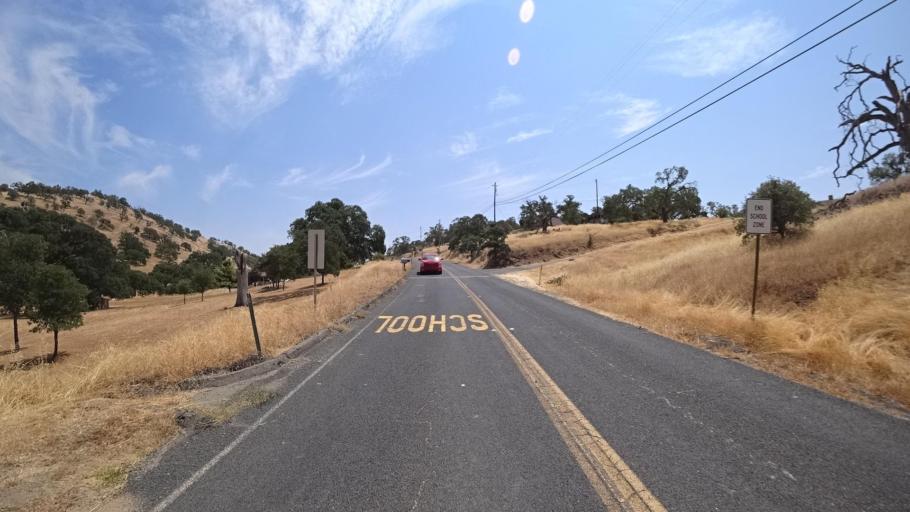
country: US
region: California
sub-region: Tuolumne County
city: Jamestown
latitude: 37.6704
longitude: -120.3571
